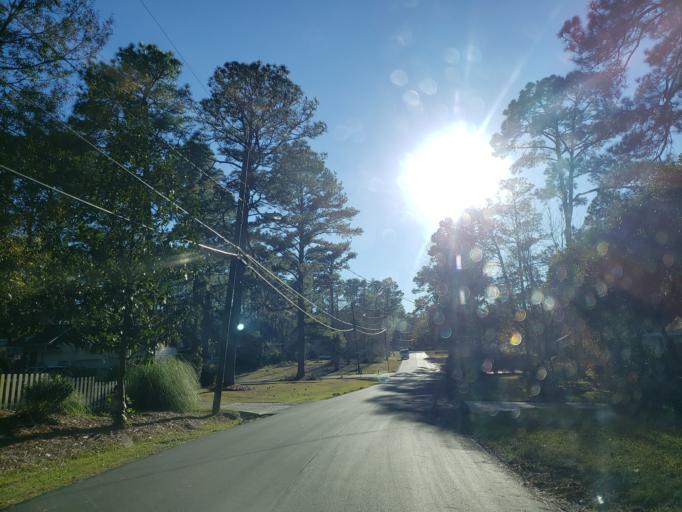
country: US
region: Mississippi
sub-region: Forrest County
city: Hattiesburg
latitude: 31.3164
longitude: -89.3197
